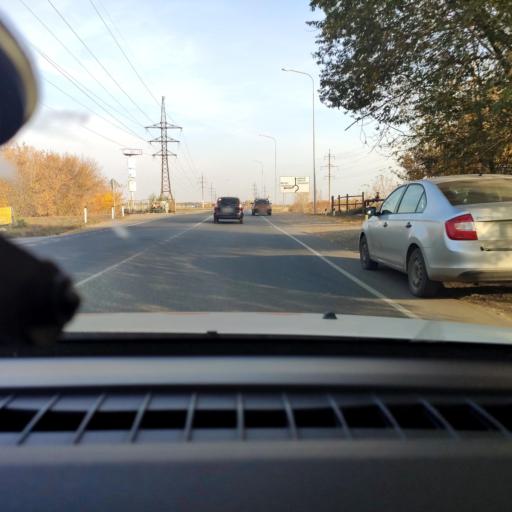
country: RU
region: Samara
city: Samara
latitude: 53.1324
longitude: 50.1349
